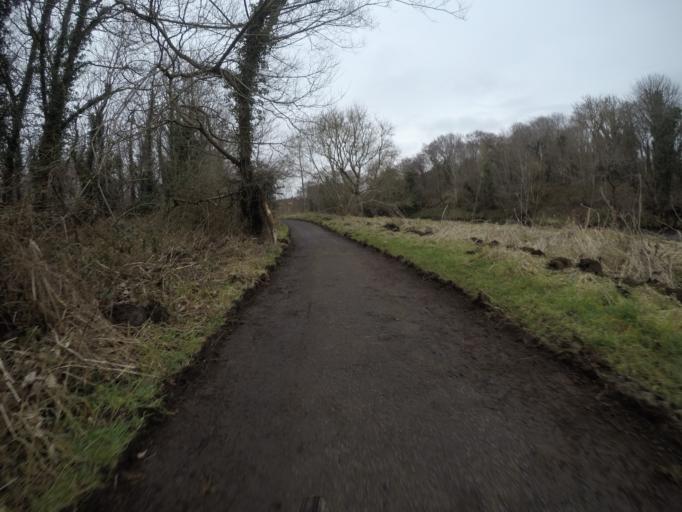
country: GB
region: Scotland
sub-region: North Ayrshire
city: Kilwinning
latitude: 55.6435
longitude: -4.6862
